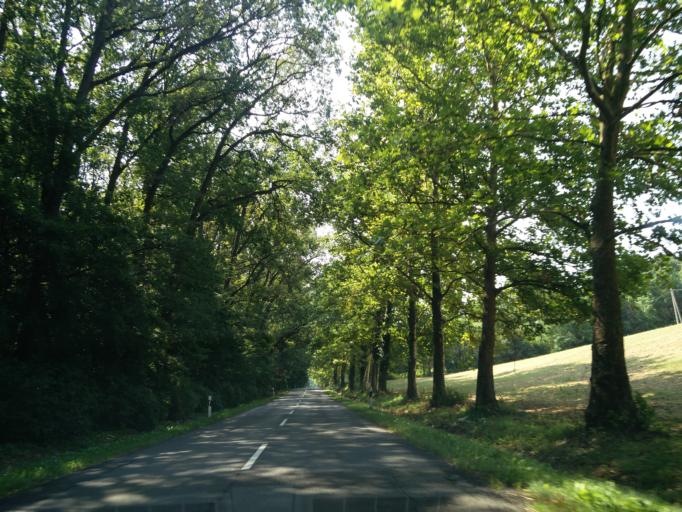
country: HU
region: Zala
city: Zalaegerszeg
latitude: 46.8115
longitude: 16.8239
